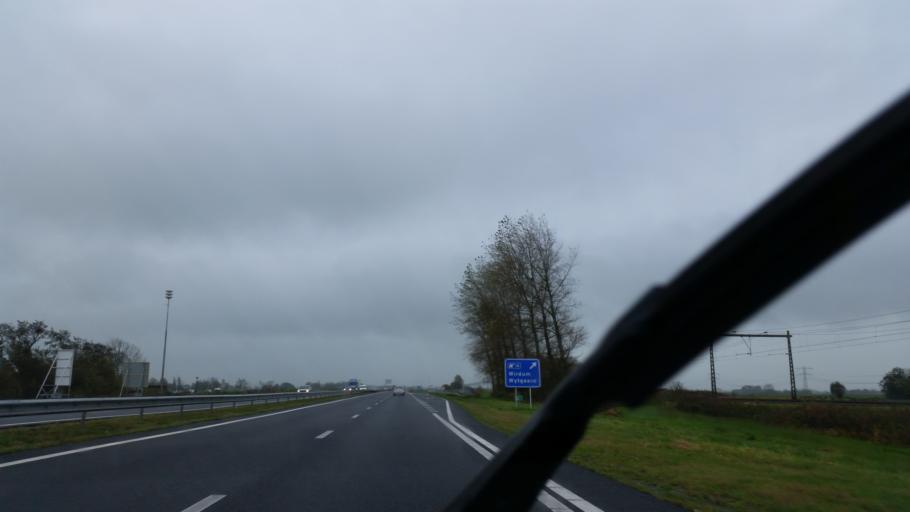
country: NL
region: Friesland
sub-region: Gemeente Leeuwarden
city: Wirdum
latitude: 53.1485
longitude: 5.7939
